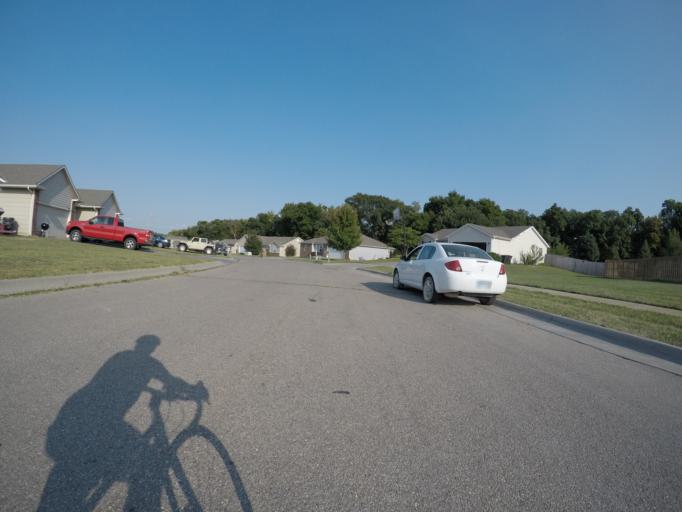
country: US
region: Kansas
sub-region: Riley County
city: Manhattan
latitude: 39.1844
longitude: -96.6413
